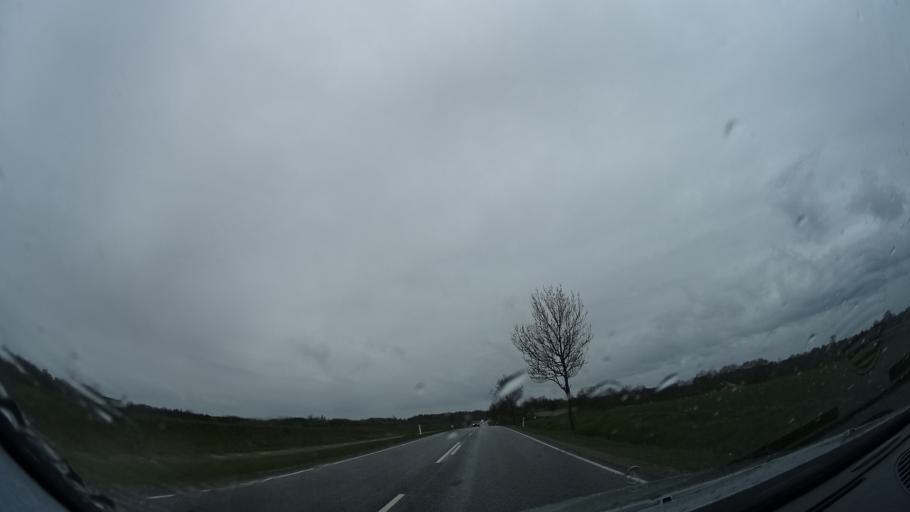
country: DK
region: Zealand
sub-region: Lejre Kommune
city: Ejby
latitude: 55.6761
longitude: 11.8352
